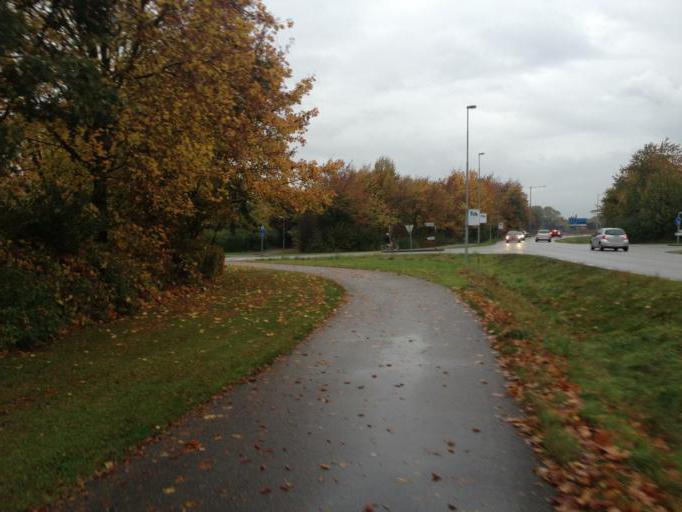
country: SE
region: Skane
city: Bjarred
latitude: 55.7244
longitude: 13.0272
